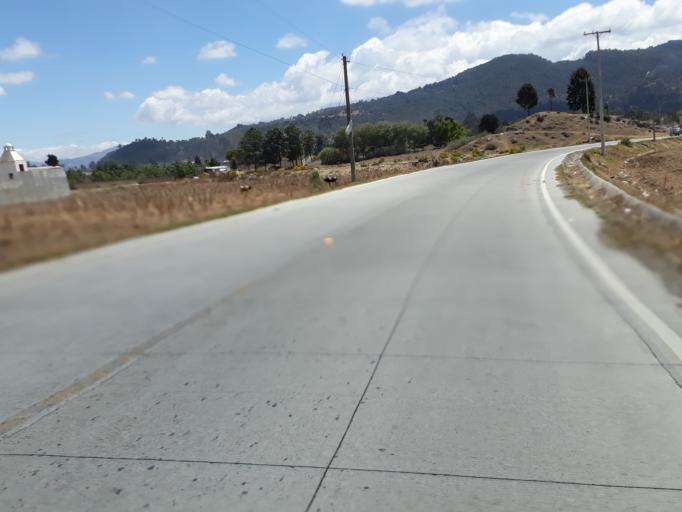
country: GT
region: Quetzaltenango
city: Quetzaltenango
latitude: 14.8156
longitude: -91.5522
